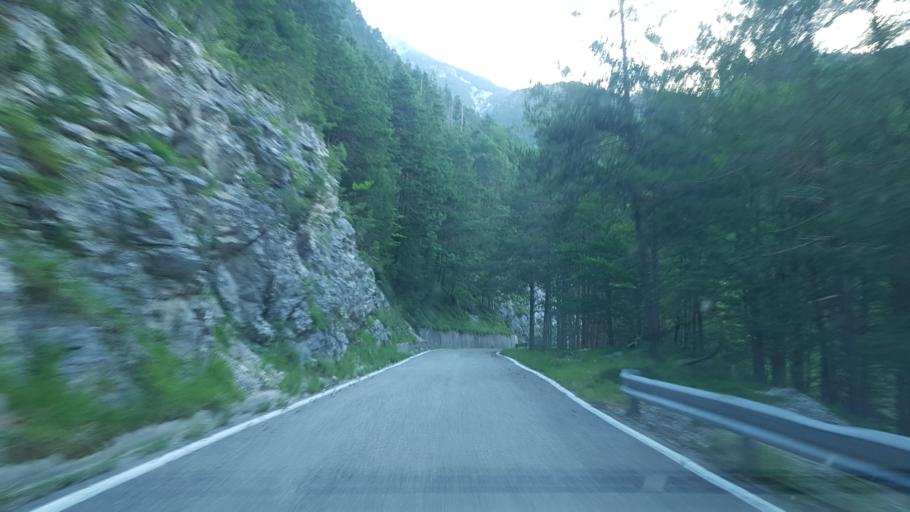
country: IT
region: Friuli Venezia Giulia
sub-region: Provincia di Udine
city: Dogna
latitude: 46.4603
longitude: 13.3816
